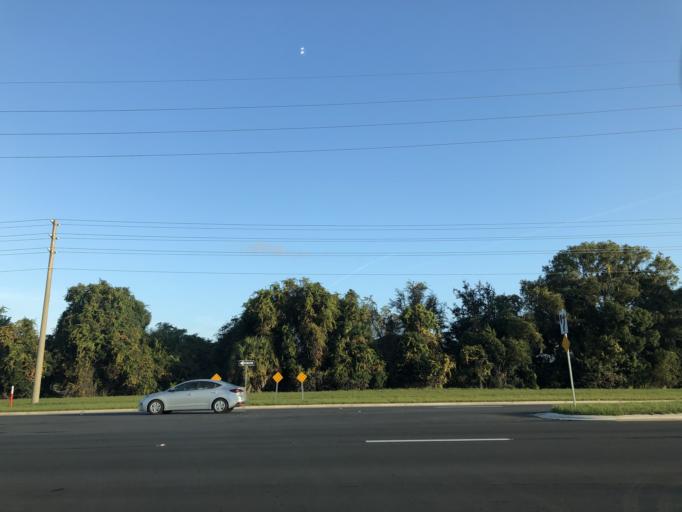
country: US
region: Florida
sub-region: Osceola County
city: Kissimmee
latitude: 28.3248
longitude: -81.4311
